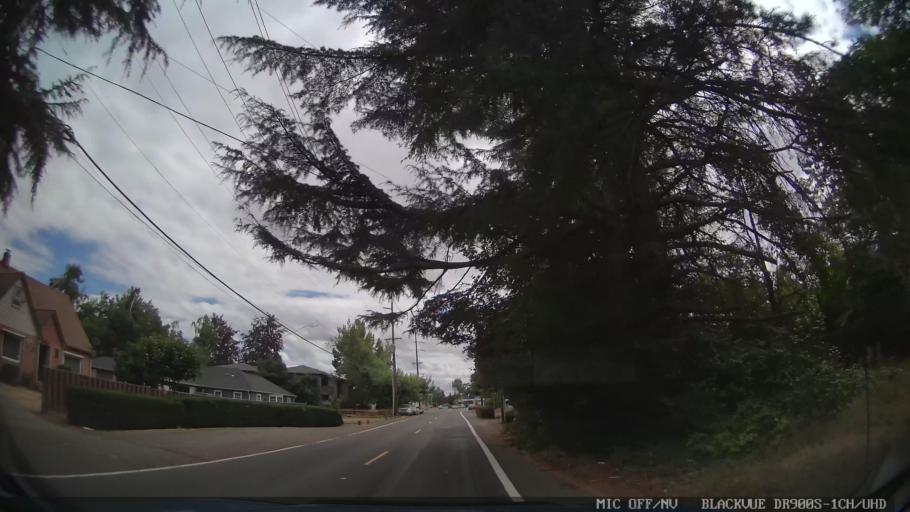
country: US
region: Oregon
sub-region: Marion County
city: Four Corners
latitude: 44.9516
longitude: -123.0010
